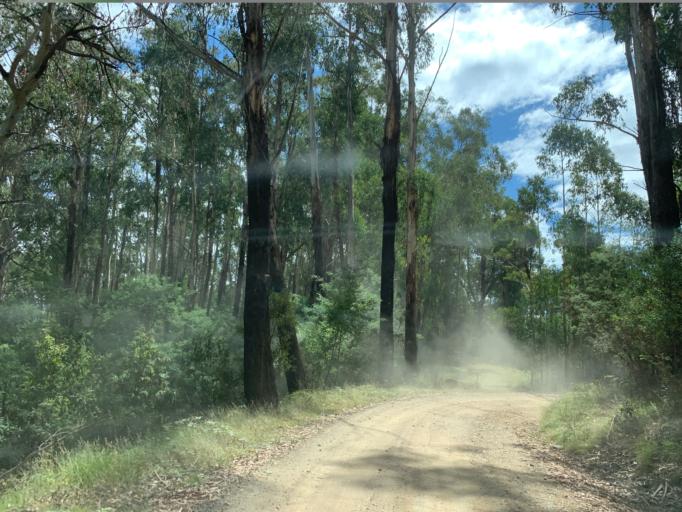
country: AU
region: Victoria
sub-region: Mansfield
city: Mansfield
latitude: -37.0915
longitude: 146.5153
